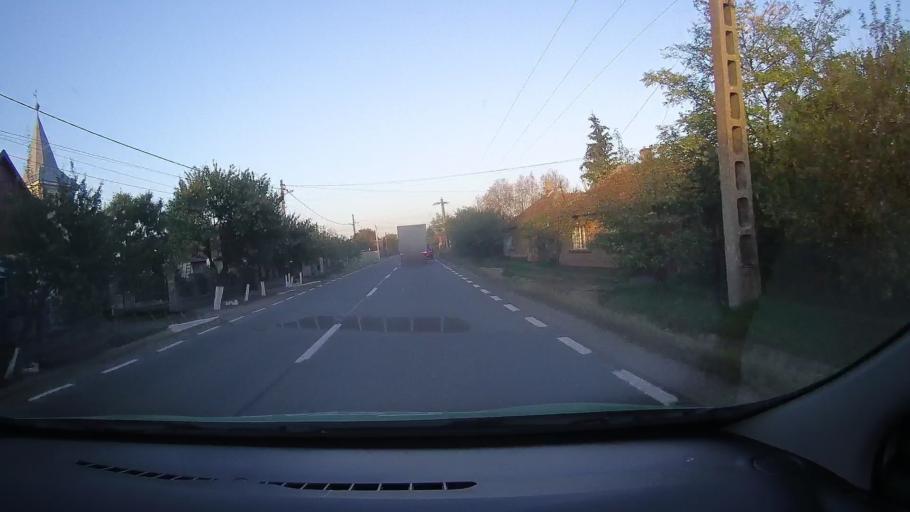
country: RO
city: Dioszeg
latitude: 47.2843
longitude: 21.9903
